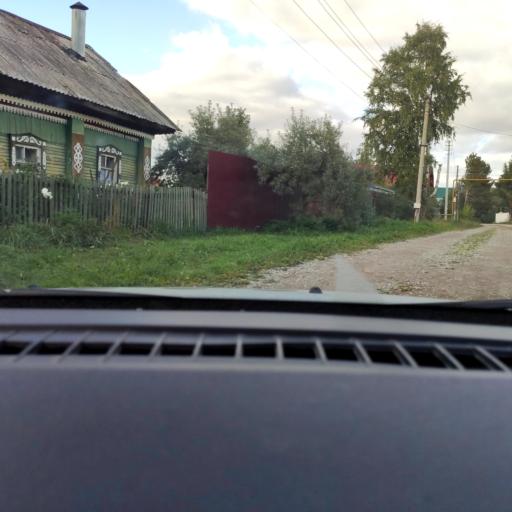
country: RU
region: Perm
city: Perm
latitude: 58.0988
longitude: 56.3714
